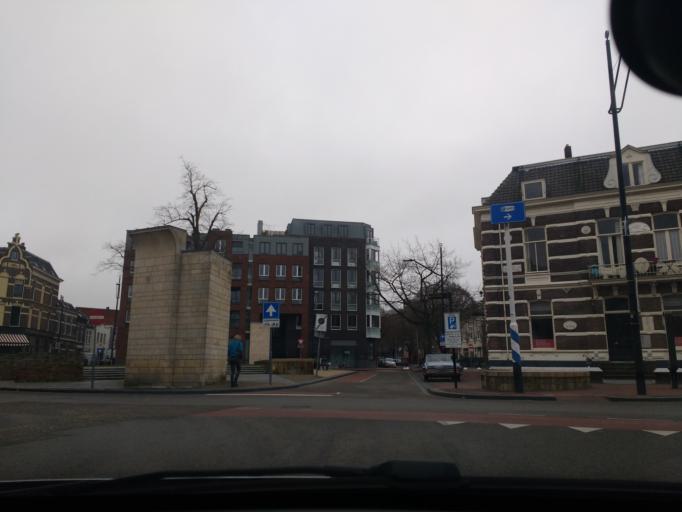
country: NL
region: Gelderland
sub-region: Gemeente Nijmegen
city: Nijmegen
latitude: 51.8442
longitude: 5.8681
